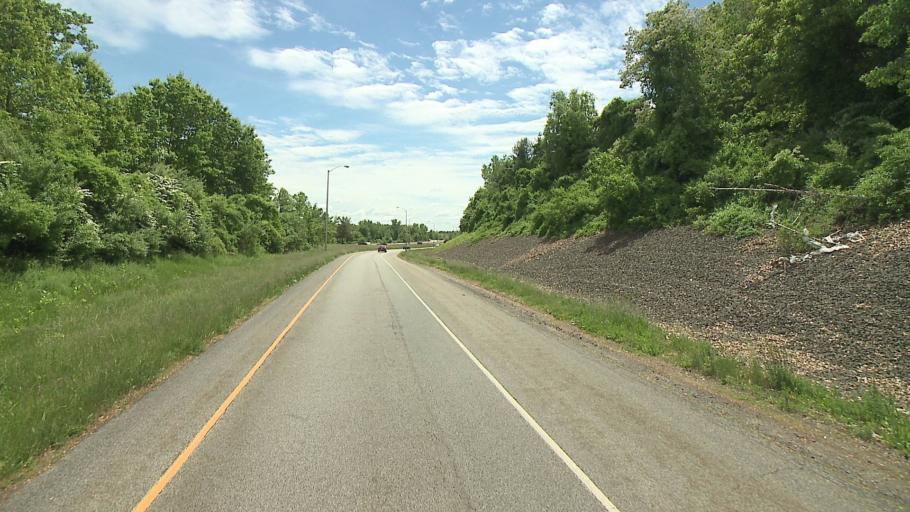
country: US
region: Connecticut
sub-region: Hartford County
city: Windsor Locks
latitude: 41.9158
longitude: -72.6305
